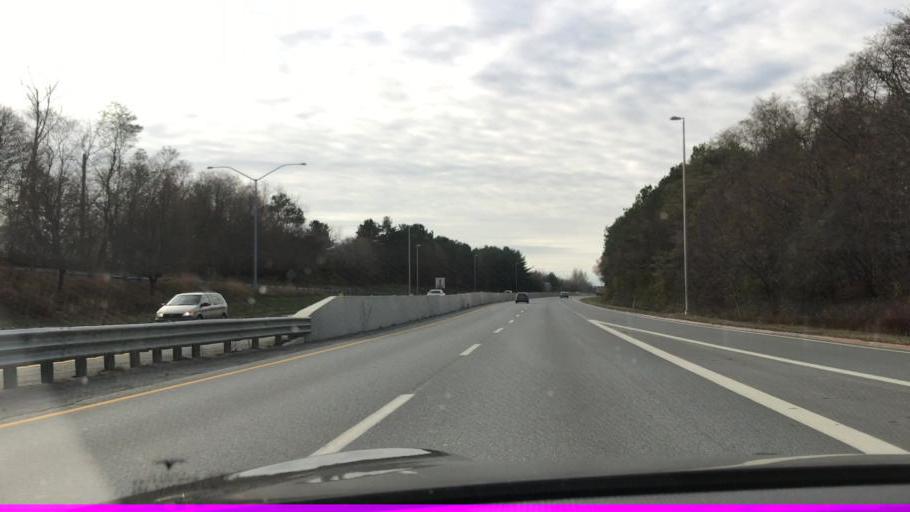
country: US
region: Maine
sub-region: Penobscot County
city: Bangor
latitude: 44.8086
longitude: -68.7936
